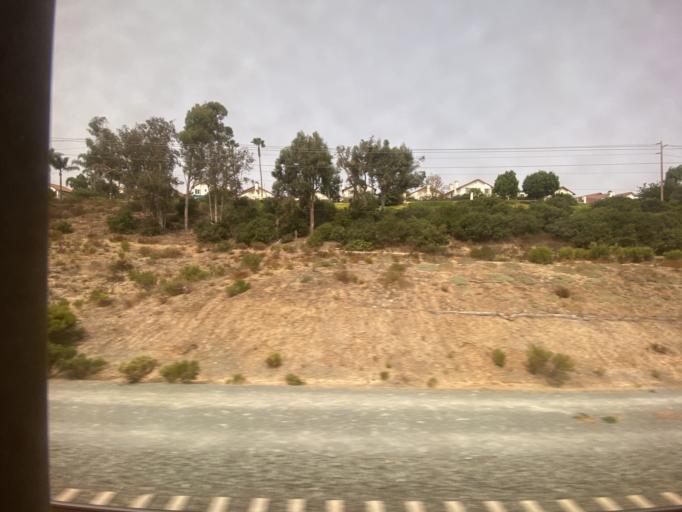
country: US
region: California
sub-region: San Diego County
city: La Jolla
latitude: 32.8567
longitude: -117.2229
